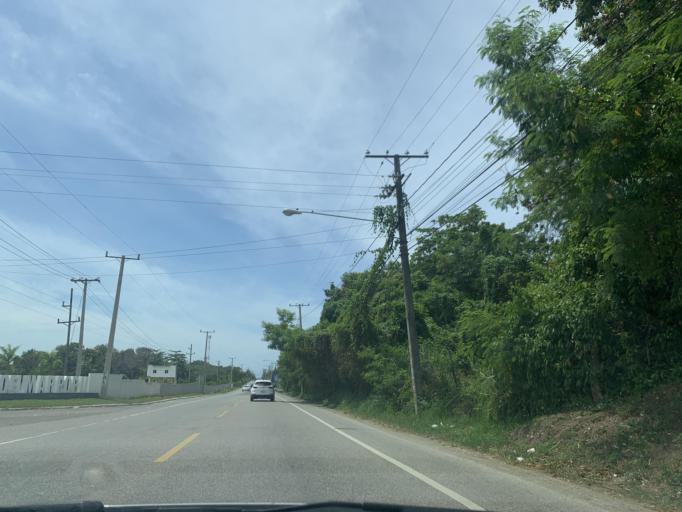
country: DO
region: Puerto Plata
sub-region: Puerto Plata
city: Puerto Plata
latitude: 19.7494
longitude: -70.6392
